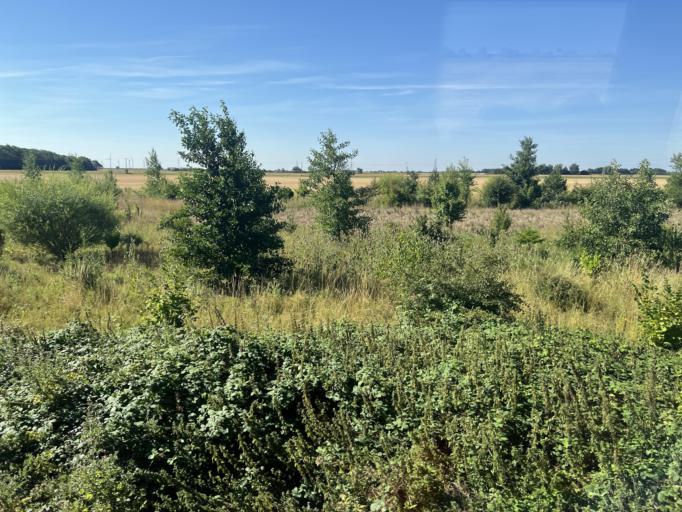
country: GB
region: England
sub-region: Lincolnshire
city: Heckington
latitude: 52.9670
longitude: -0.2379
